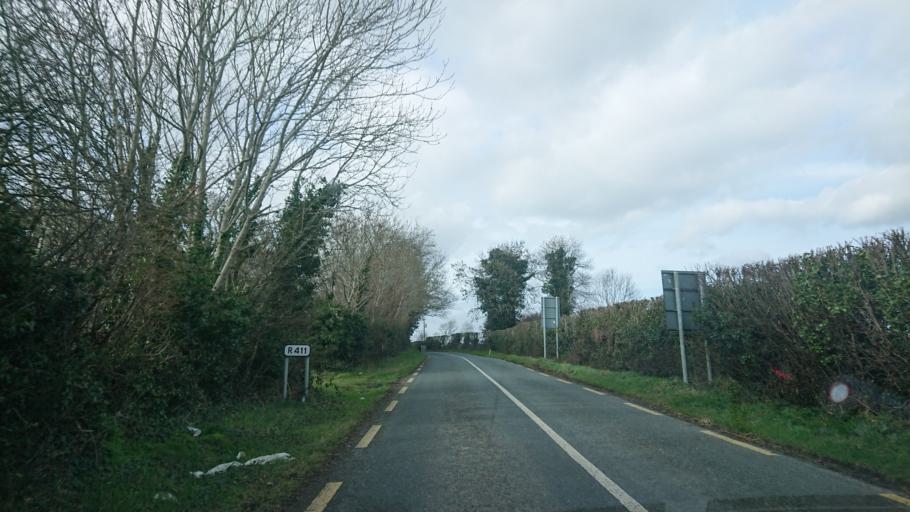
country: IE
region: Leinster
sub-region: Kildare
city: Naas
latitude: 53.1891
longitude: -6.6438
